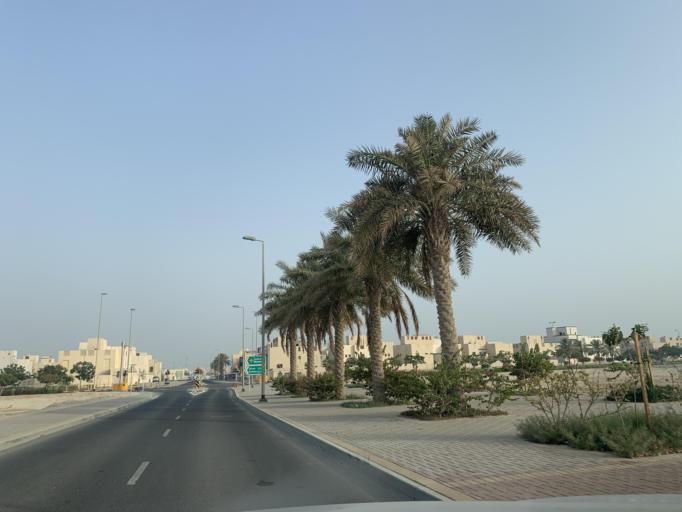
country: BH
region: Manama
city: Jidd Hafs
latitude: 26.2258
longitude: 50.4461
